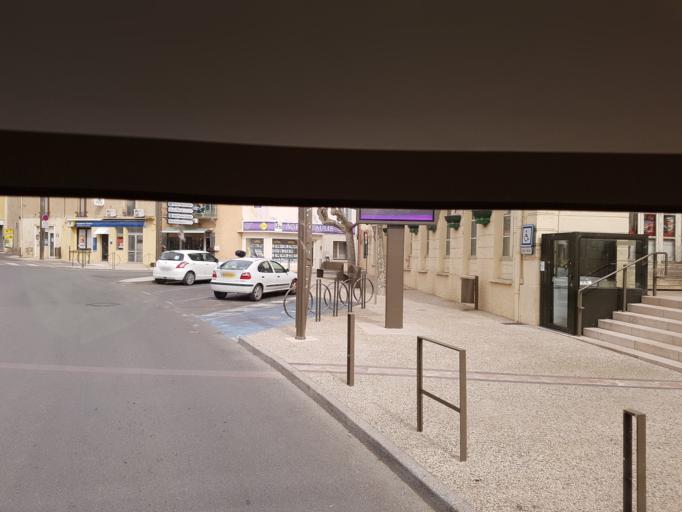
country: FR
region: Languedoc-Roussillon
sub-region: Departement de l'Aude
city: Fleury
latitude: 43.2287
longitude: 3.1350
